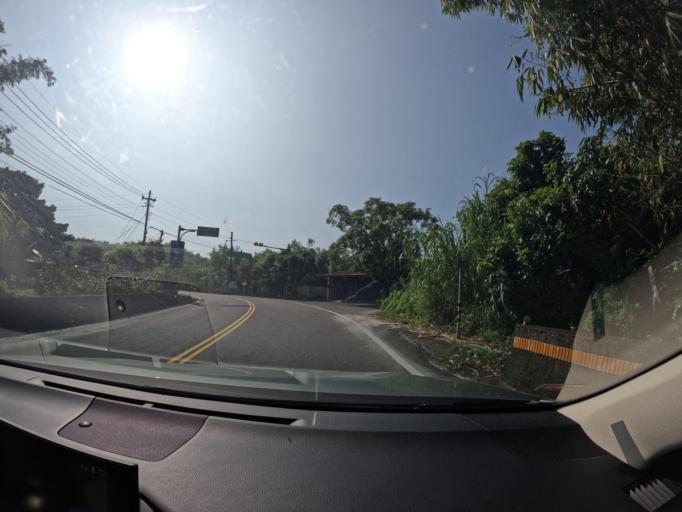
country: TW
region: Taiwan
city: Yujing
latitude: 23.0670
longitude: 120.5542
